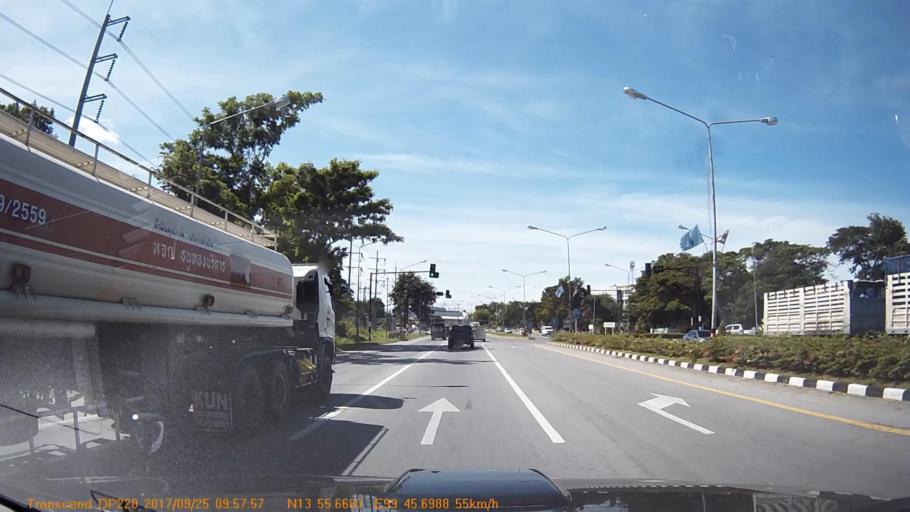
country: TH
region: Kanchanaburi
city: Tha Maka
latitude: 13.9274
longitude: 99.7617
